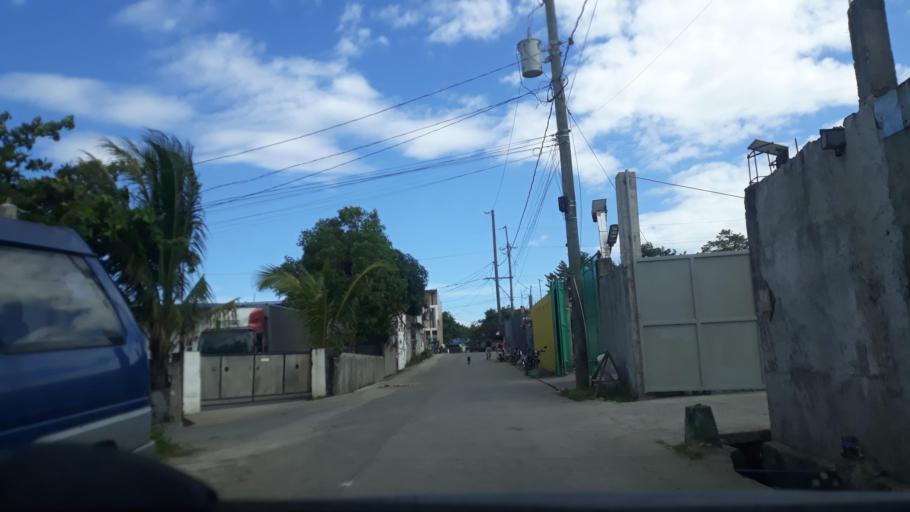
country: PH
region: Calabarzon
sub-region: Province of Cavite
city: Bulihan
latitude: 14.3043
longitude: 120.9738
